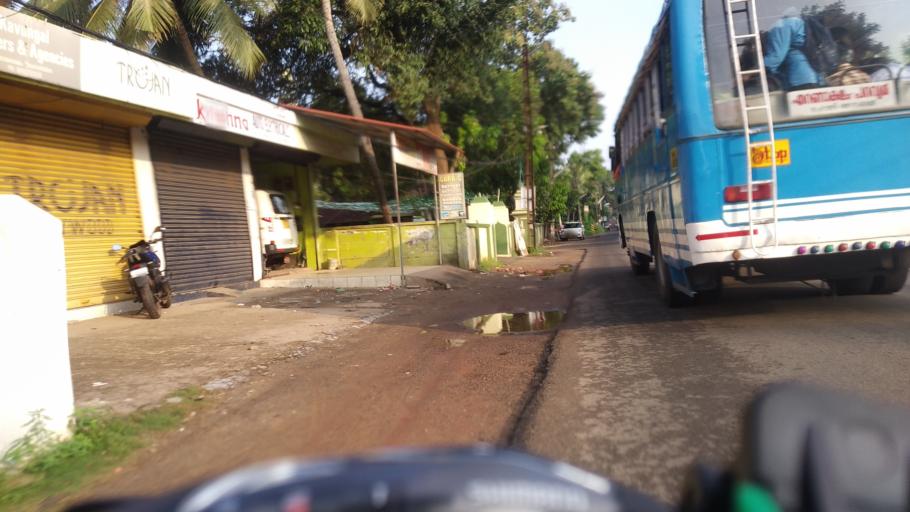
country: IN
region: Kerala
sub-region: Ernakulam
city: Elur
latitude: 10.0763
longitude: 76.2111
